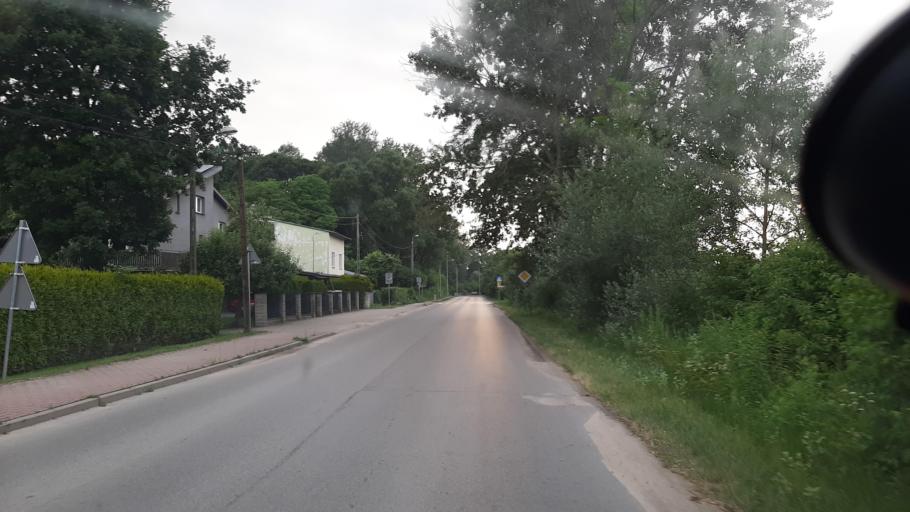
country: PL
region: Lublin Voivodeship
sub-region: Powiat lubelski
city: Garbow
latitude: 51.3501
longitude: 22.3347
